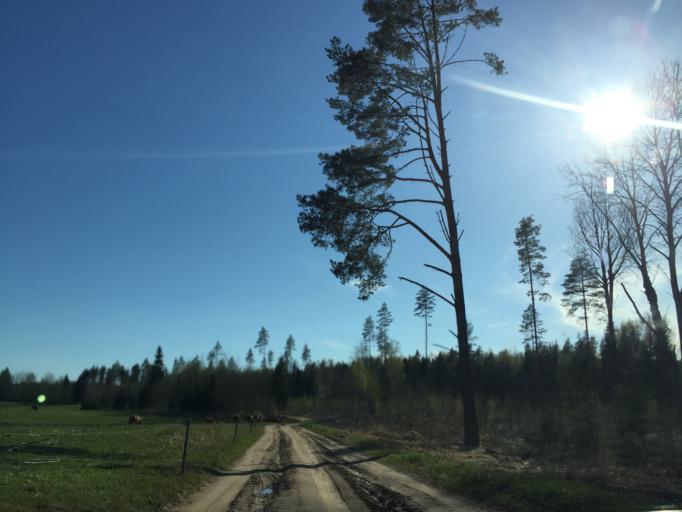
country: EE
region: Valgamaa
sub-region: Valga linn
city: Valga
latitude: 57.7808
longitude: 26.2350
